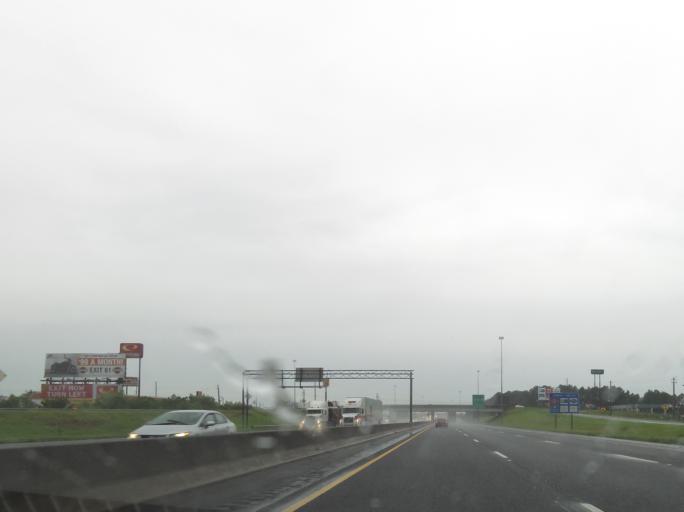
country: US
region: Georgia
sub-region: Tift County
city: Tifton
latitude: 31.4605
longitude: -83.5301
